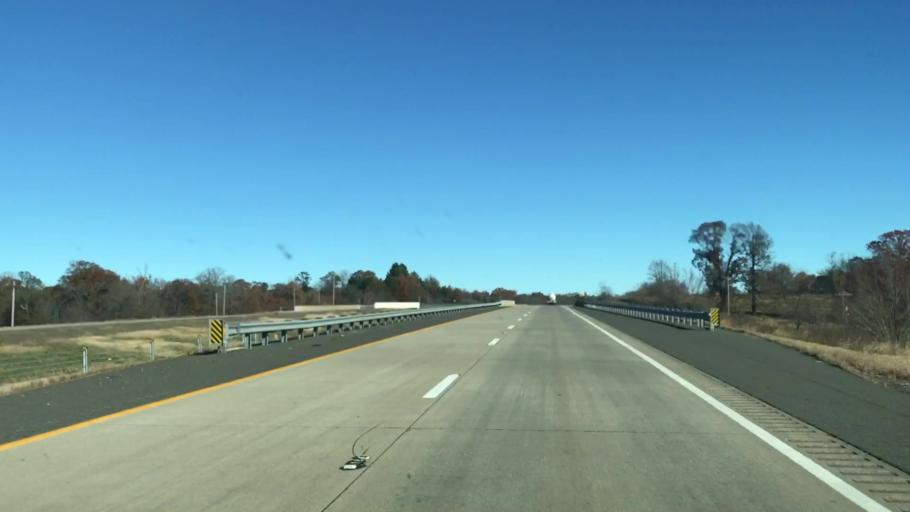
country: US
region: Texas
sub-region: Cass County
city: Queen City
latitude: 33.1520
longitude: -93.8903
